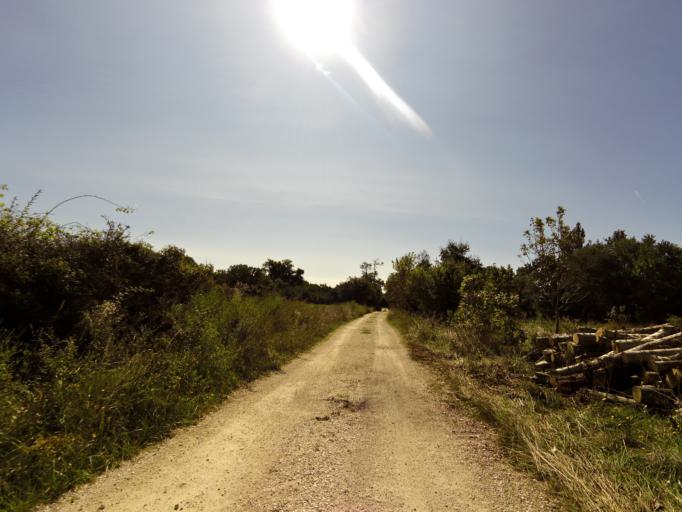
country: HU
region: Veszprem
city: Tapolca
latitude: 46.8373
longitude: 17.3973
